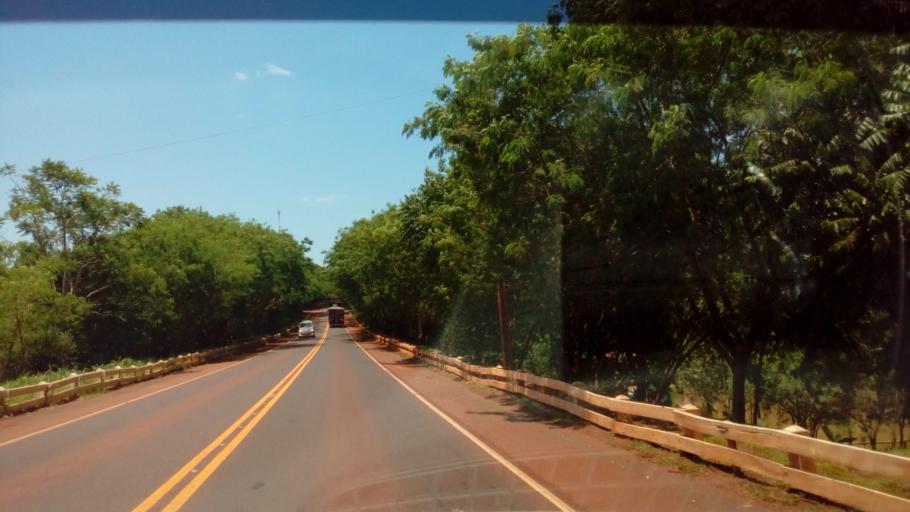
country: PY
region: Alto Parana
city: Santa Rita
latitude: -25.8323
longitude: -55.1155
